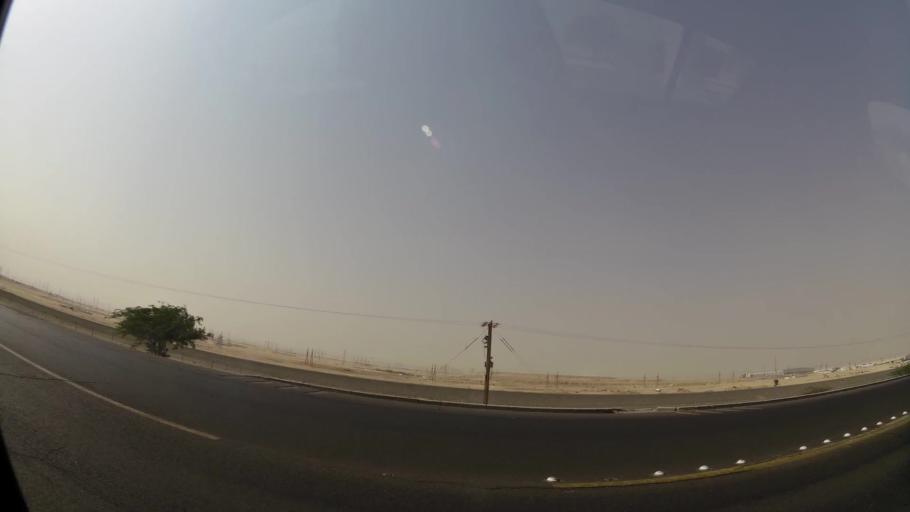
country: KW
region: Muhafazat al Jahra'
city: Al Jahra'
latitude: 29.3303
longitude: 47.6333
